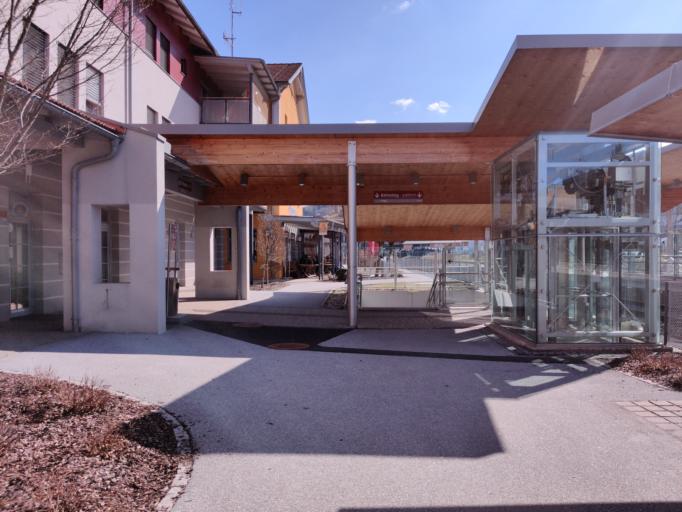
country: AT
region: Styria
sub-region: Politischer Bezirk Voitsberg
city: Voitsberg
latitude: 47.0434
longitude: 15.1501
